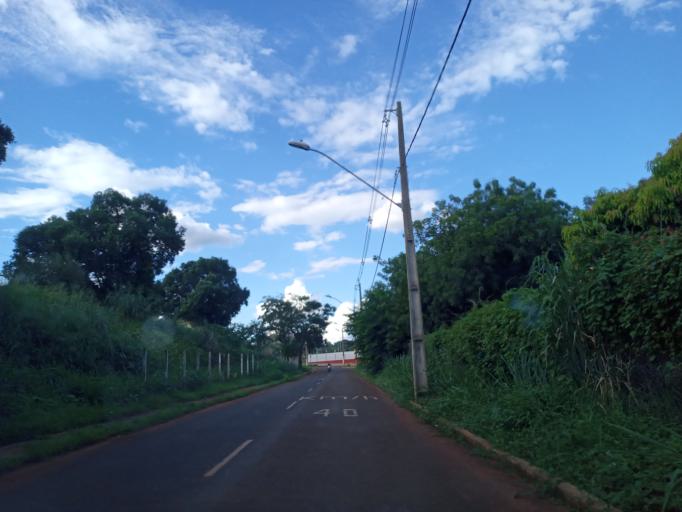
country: BR
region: Minas Gerais
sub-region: Ituiutaba
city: Ituiutaba
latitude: -18.9684
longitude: -49.4905
